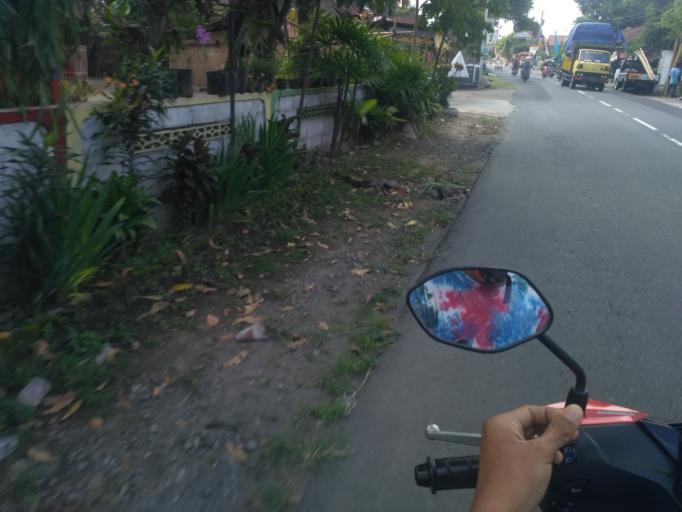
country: ID
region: Daerah Istimewa Yogyakarta
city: Godean
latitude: -7.7508
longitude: 110.3204
